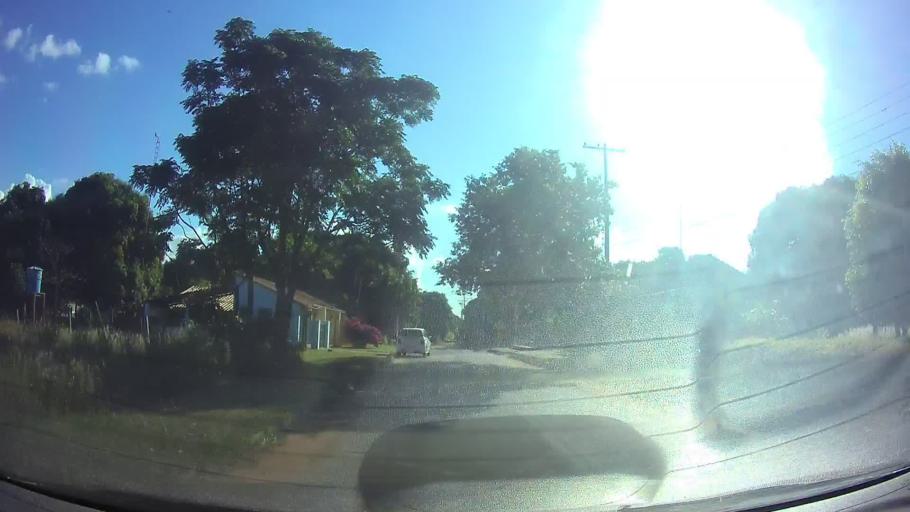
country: PY
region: Central
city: Aregua
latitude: -25.3362
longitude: -57.3849
